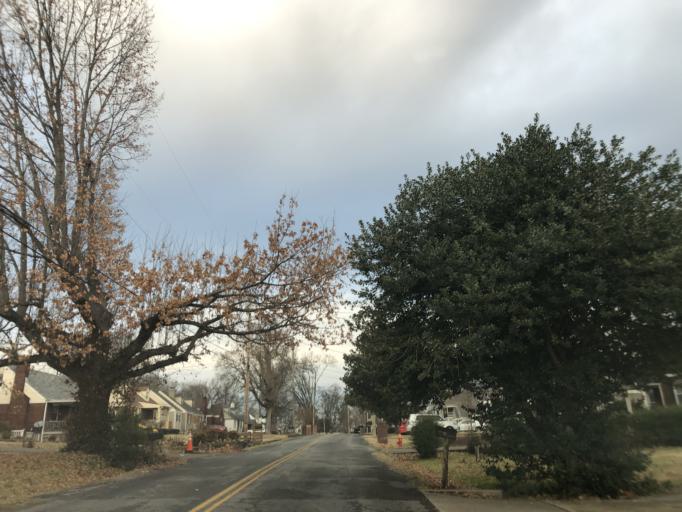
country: US
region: Tennessee
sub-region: Davidson County
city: Nashville
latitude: 36.1993
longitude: -86.7372
